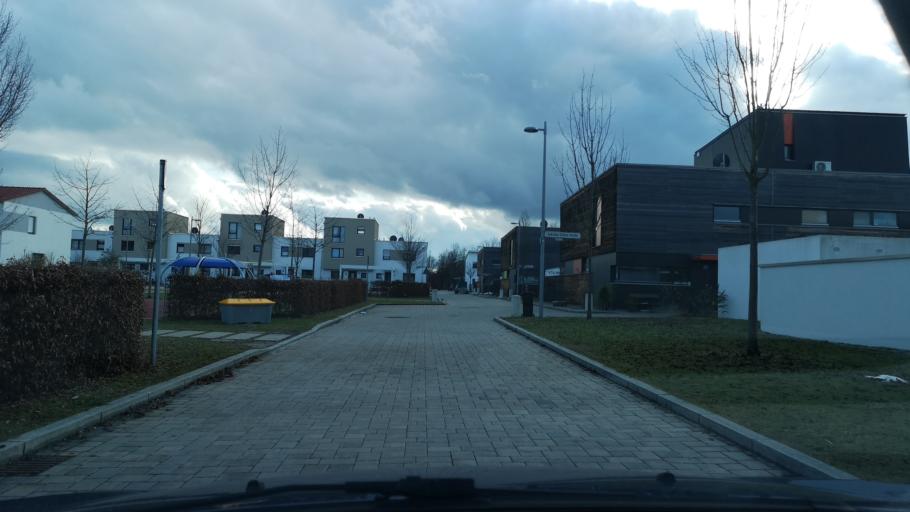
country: DE
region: Bavaria
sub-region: Upper Bavaria
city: Pliening
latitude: 48.1786
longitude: 11.8005
